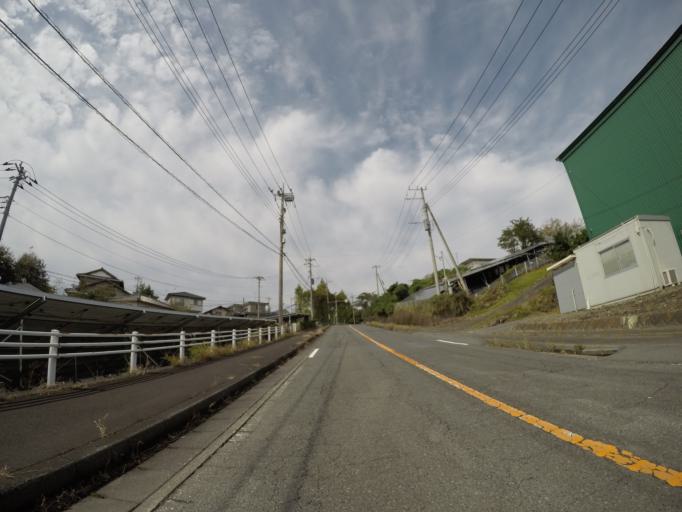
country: JP
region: Shizuoka
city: Fuji
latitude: 35.1936
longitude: 138.6977
